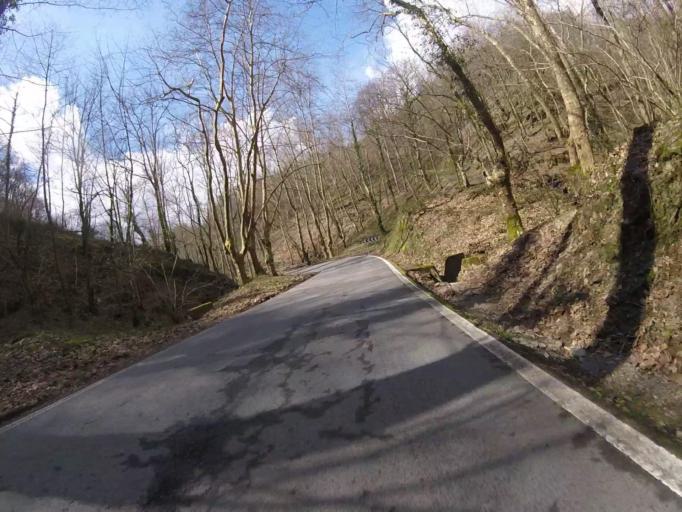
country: ES
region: Navarre
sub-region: Provincia de Navarra
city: Etxalar
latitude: 43.2425
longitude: -1.6296
